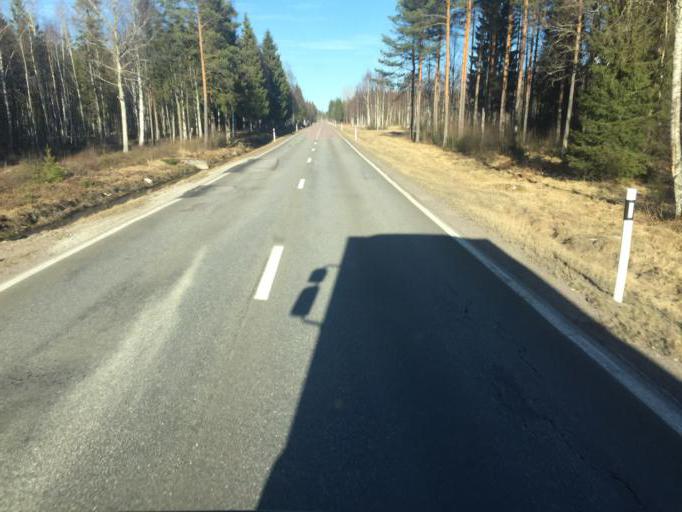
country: SE
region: Dalarna
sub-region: Vansbro Kommun
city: Jarna
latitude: 60.4457
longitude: 14.5390
